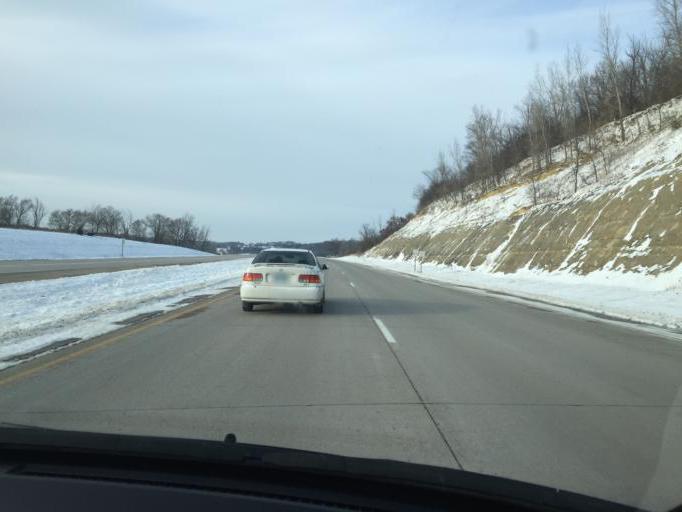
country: US
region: Minnesota
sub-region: Olmsted County
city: Rochester
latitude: 44.0223
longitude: -92.4195
